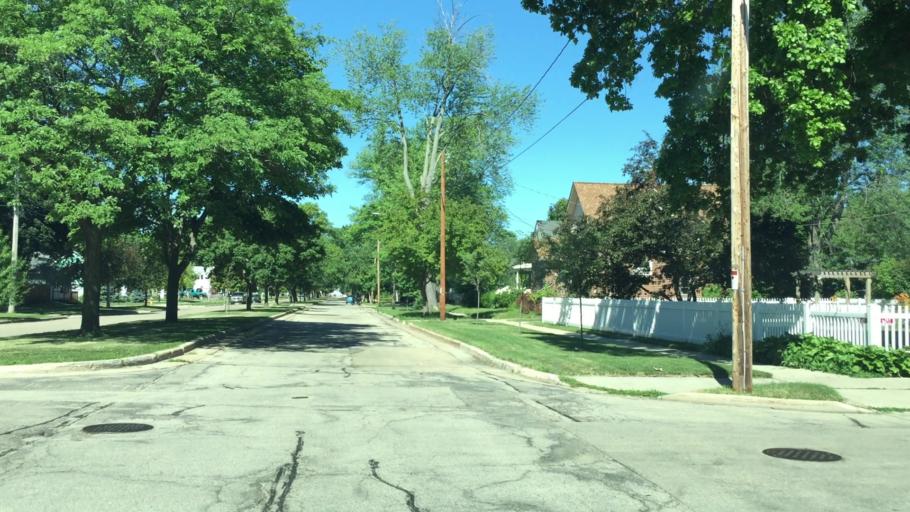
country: US
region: Wisconsin
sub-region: Winnebago County
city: Menasha
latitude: 44.1936
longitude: -88.4444
